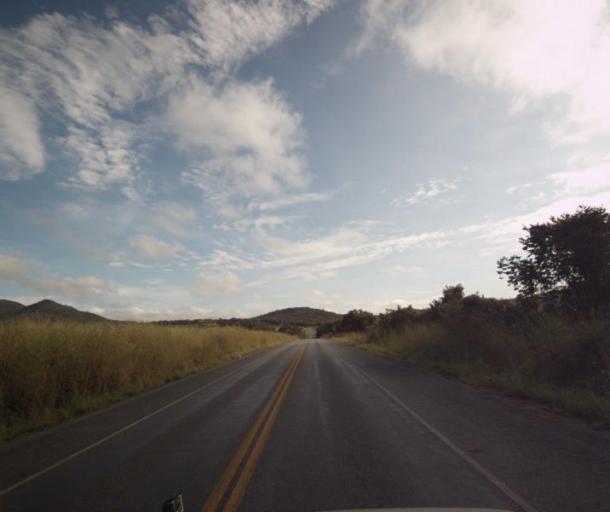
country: BR
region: Goias
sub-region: Pirenopolis
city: Pirenopolis
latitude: -15.5436
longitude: -48.6227
